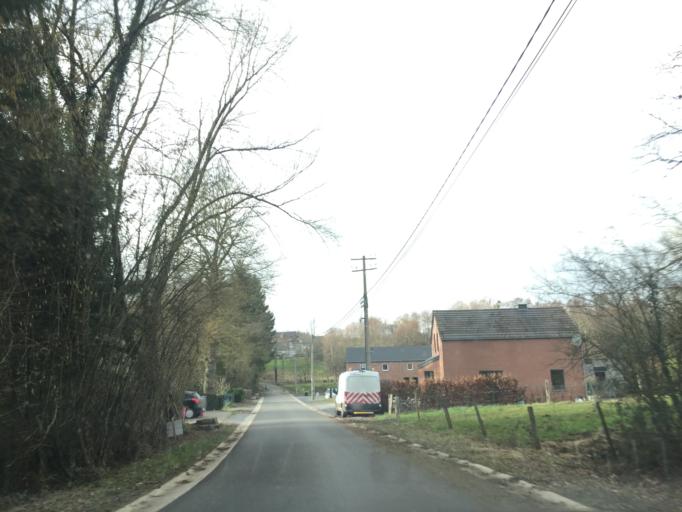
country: BE
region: Wallonia
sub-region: Province du Luxembourg
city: Durbuy
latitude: 50.3071
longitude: 5.4869
